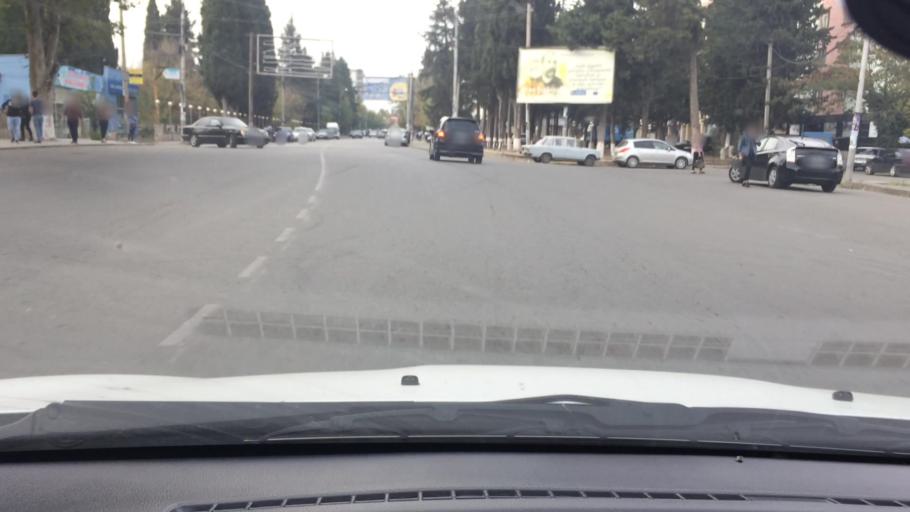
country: GE
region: Kvemo Kartli
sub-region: Marneuli
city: Marneuli
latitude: 41.4732
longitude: 44.8144
